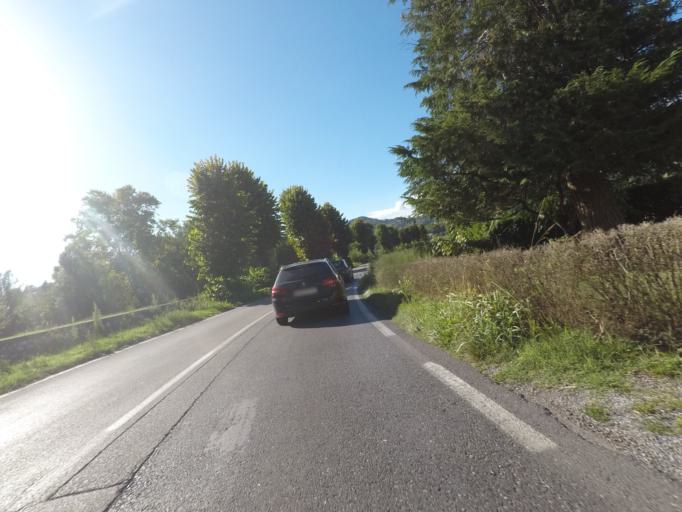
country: IT
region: Tuscany
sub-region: Provincia di Lucca
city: Lucca
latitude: 43.8767
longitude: 10.4889
